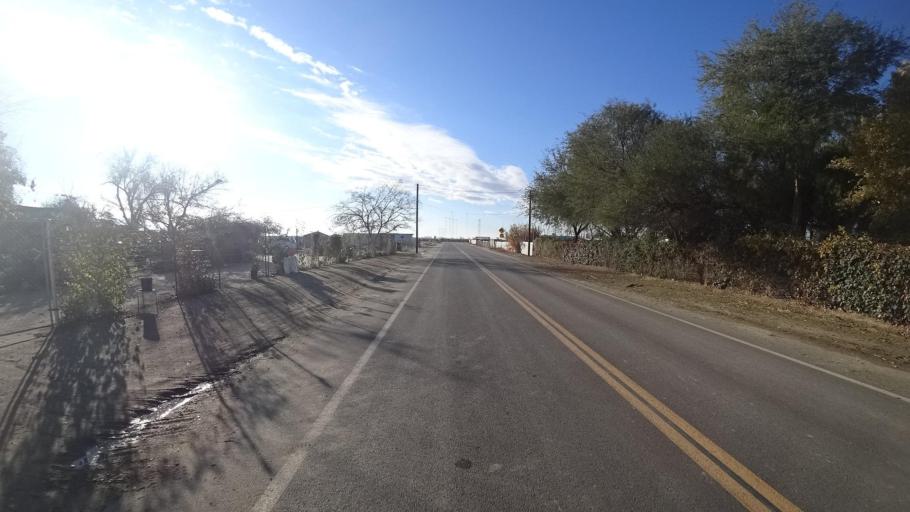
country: US
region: California
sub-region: Kern County
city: Delano
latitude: 35.7703
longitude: -119.2830
